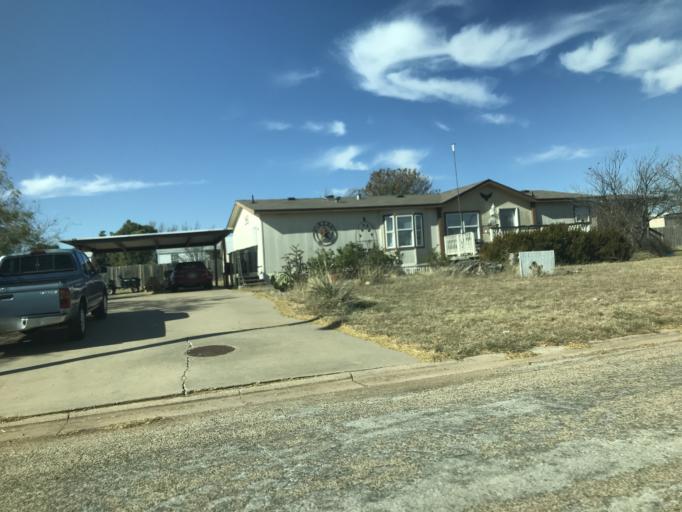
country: US
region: Texas
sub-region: Taylor County
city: Abilene
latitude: 32.5007
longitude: -99.7598
